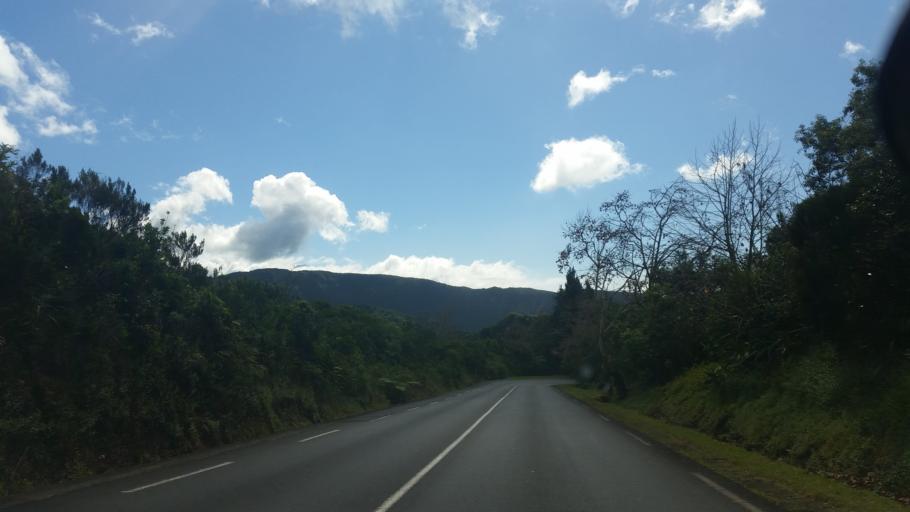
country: RE
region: Reunion
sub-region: Reunion
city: Saint-Benoit
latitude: -21.1130
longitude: 55.6566
